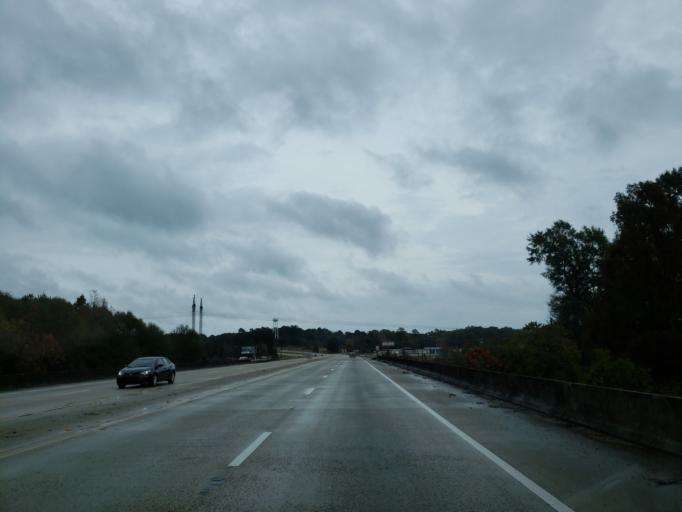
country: US
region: Mississippi
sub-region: Jones County
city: Laurel
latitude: 31.6973
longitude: -89.1094
